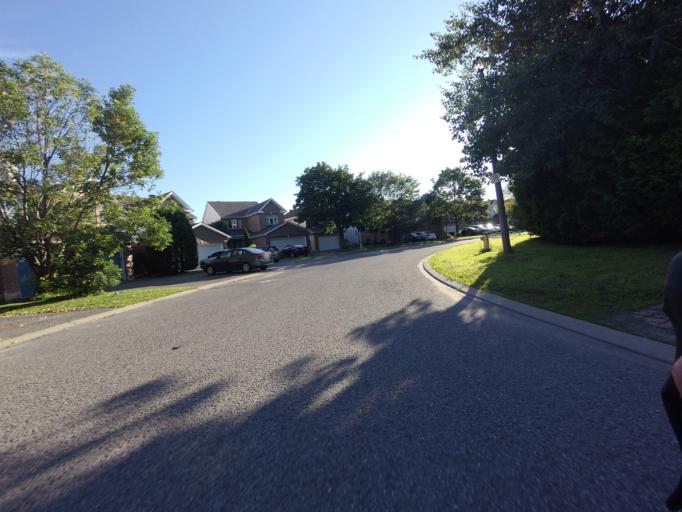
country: CA
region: Ontario
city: Bells Corners
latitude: 45.2871
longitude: -75.7393
